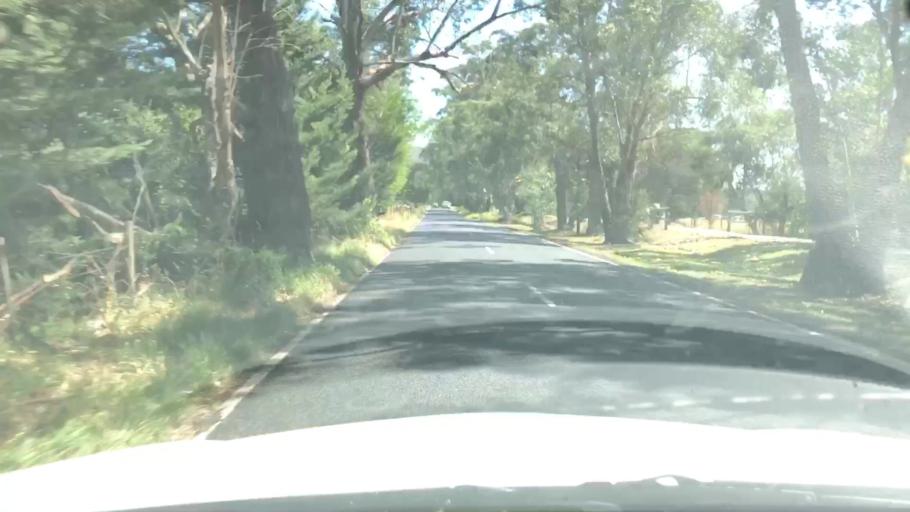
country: AU
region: Victoria
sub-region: Yarra Ranges
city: Yarra Junction
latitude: -37.7704
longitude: 145.6317
